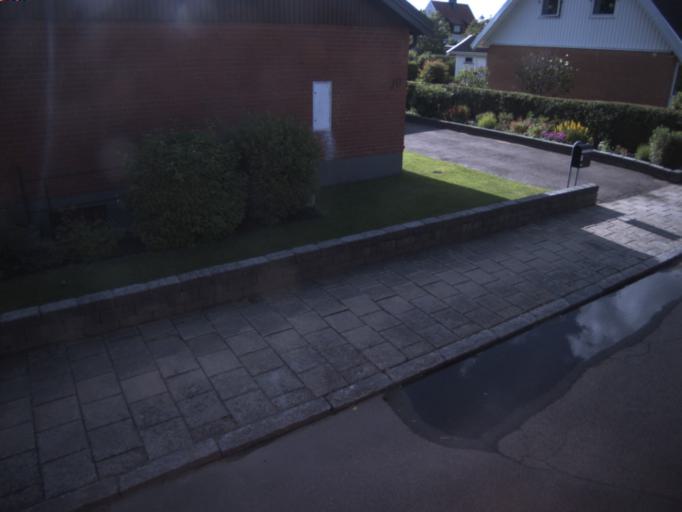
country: SE
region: Skane
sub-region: Helsingborg
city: Helsingborg
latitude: 56.0376
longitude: 12.7265
